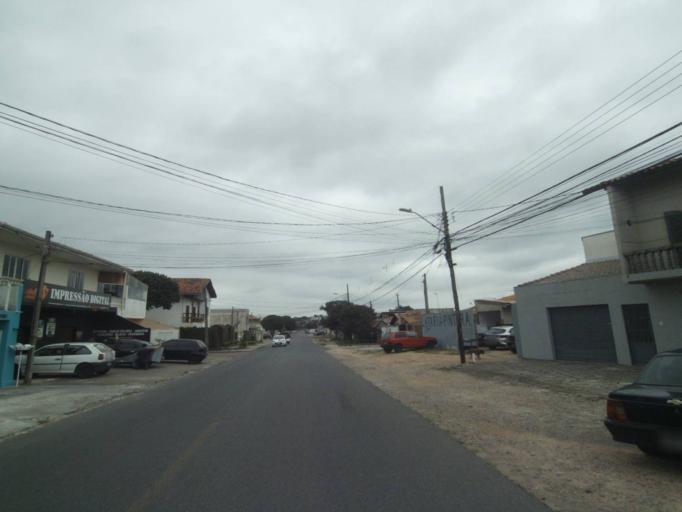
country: BR
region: Parana
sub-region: Sao Jose Dos Pinhais
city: Sao Jose dos Pinhais
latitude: -25.5419
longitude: -49.2561
